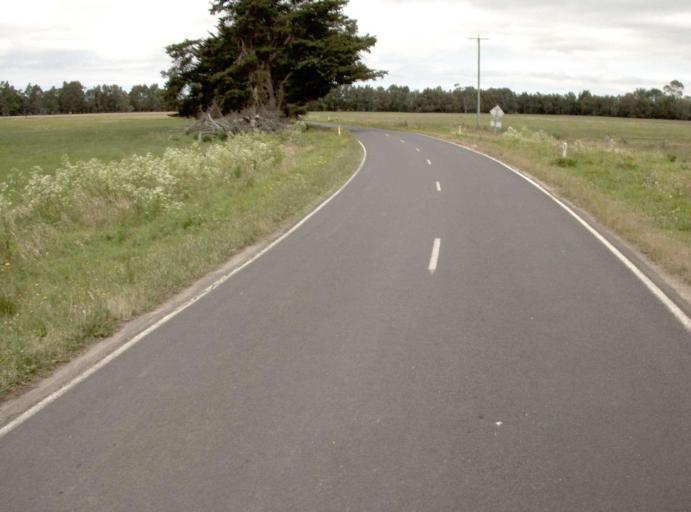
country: AU
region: Victoria
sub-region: Latrobe
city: Traralgon
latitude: -38.5051
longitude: 146.6643
